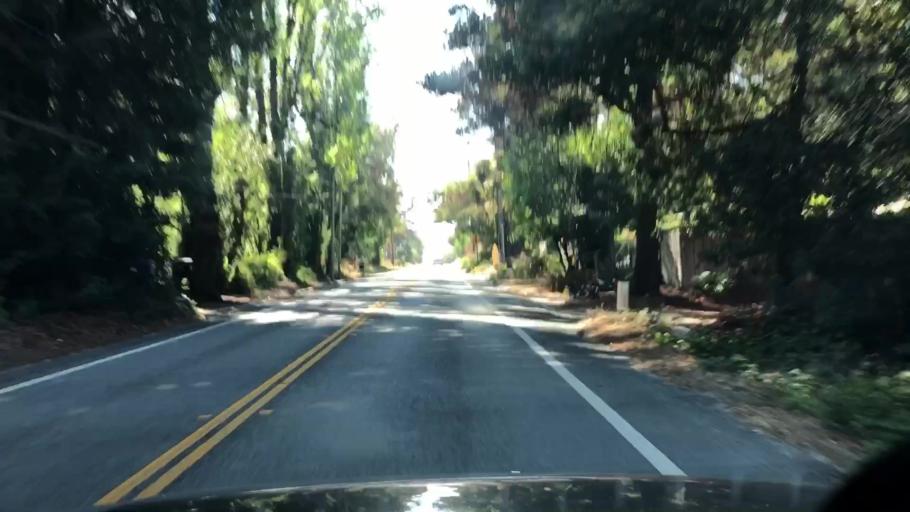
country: US
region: California
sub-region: Santa Cruz County
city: Aptos Hills-Larkin Valley
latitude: 36.9878
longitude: -121.8392
